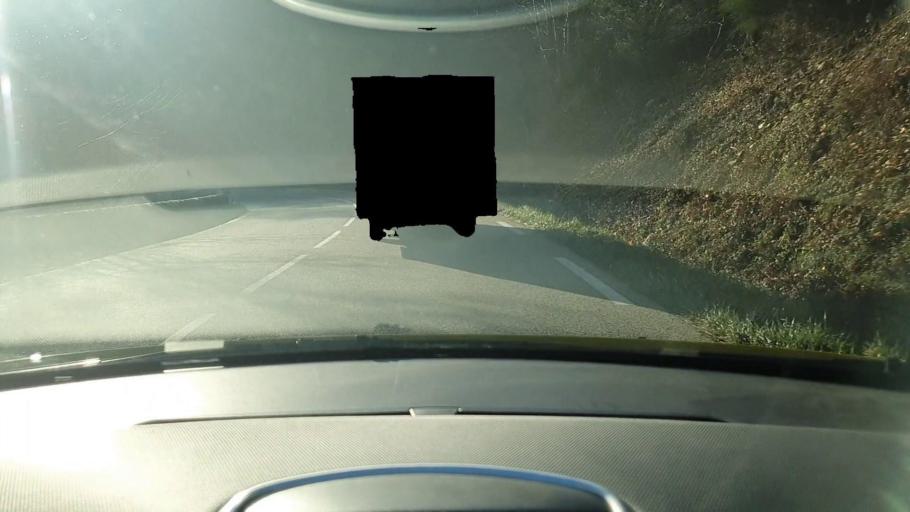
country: FR
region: Languedoc-Roussillon
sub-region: Departement du Gard
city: Branoux-les-Taillades
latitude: 44.3590
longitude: 3.9513
